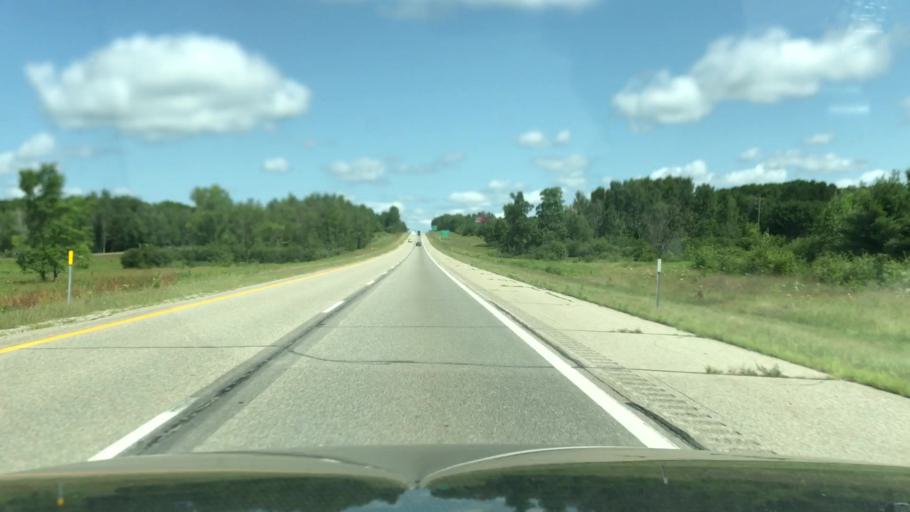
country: US
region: Michigan
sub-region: Mecosta County
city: Big Rapids
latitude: 43.7157
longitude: -85.5302
